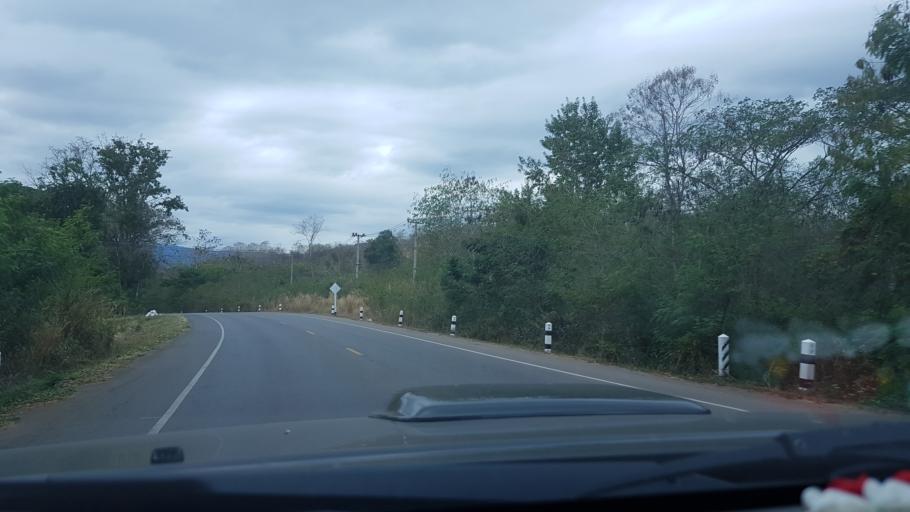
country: TH
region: Phetchabun
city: Phetchabun
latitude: 16.5336
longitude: 101.1065
